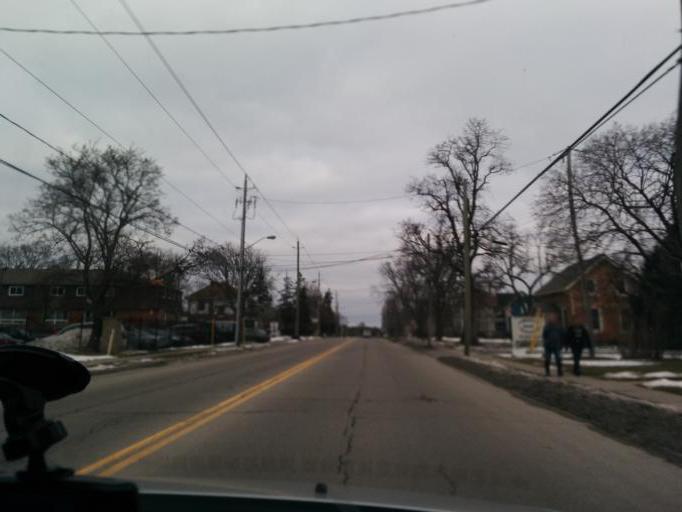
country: CA
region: Ontario
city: Ancaster
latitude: 42.9667
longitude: -80.0475
